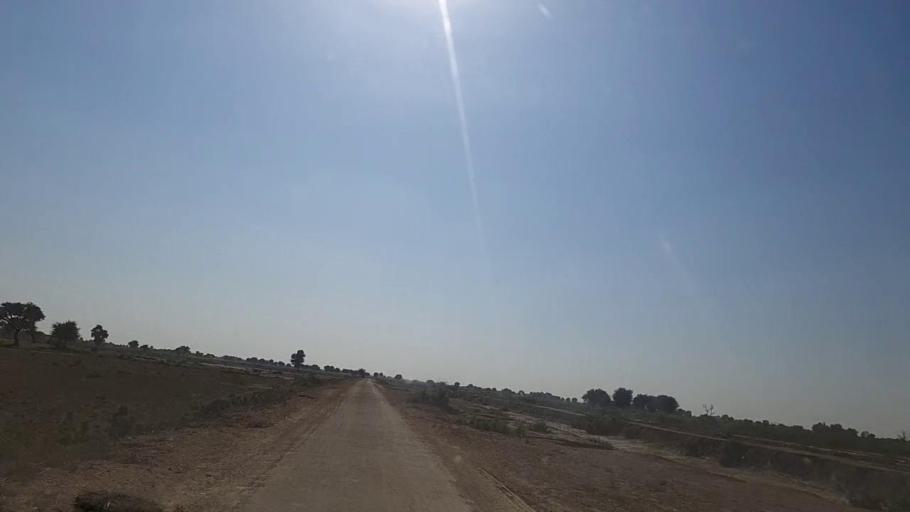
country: PK
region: Sindh
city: Digri
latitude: 25.1242
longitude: 69.0520
